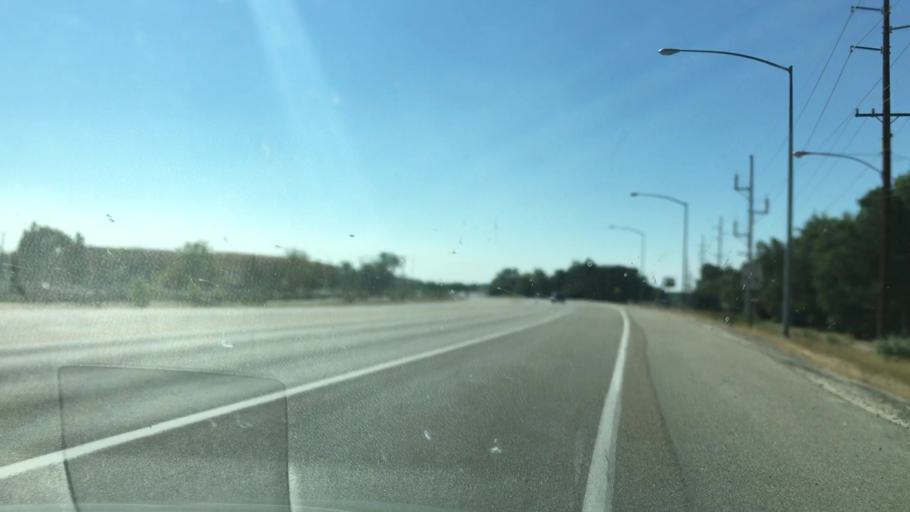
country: US
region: Idaho
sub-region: Ada County
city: Eagle
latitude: 43.6851
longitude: -116.3211
